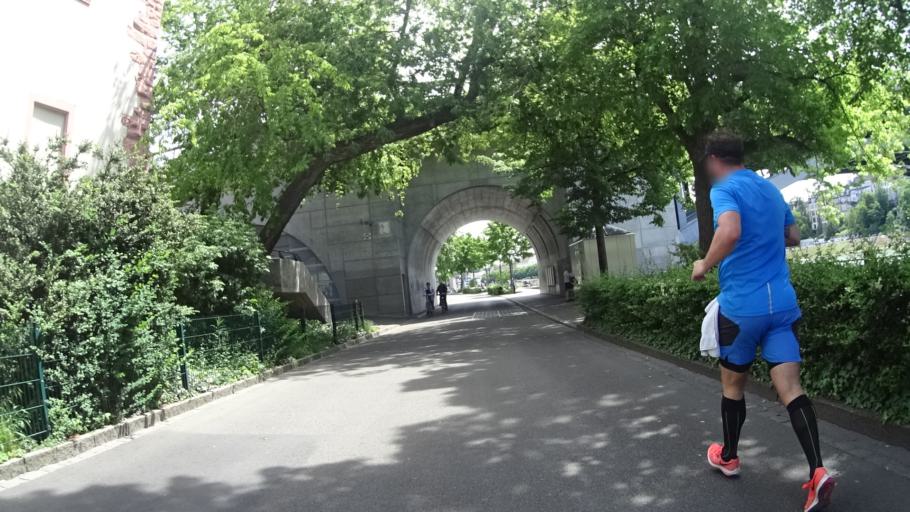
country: CH
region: Basel-City
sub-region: Basel-Stadt
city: Basel
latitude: 47.5575
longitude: 7.5964
